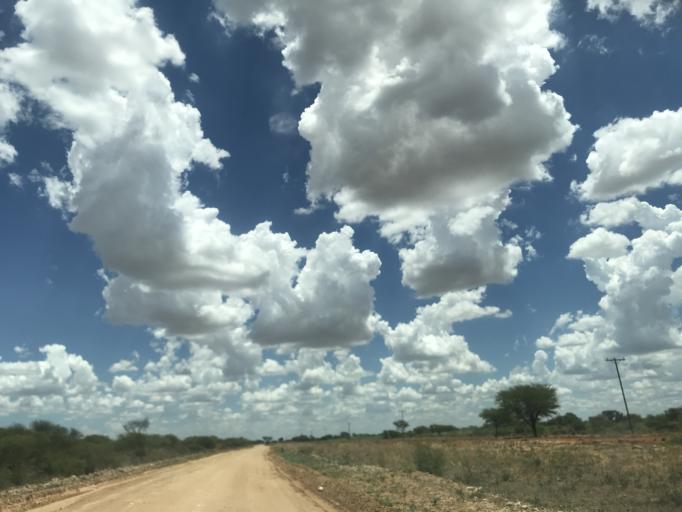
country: BW
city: Mabuli
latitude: -25.7914
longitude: 24.6540
